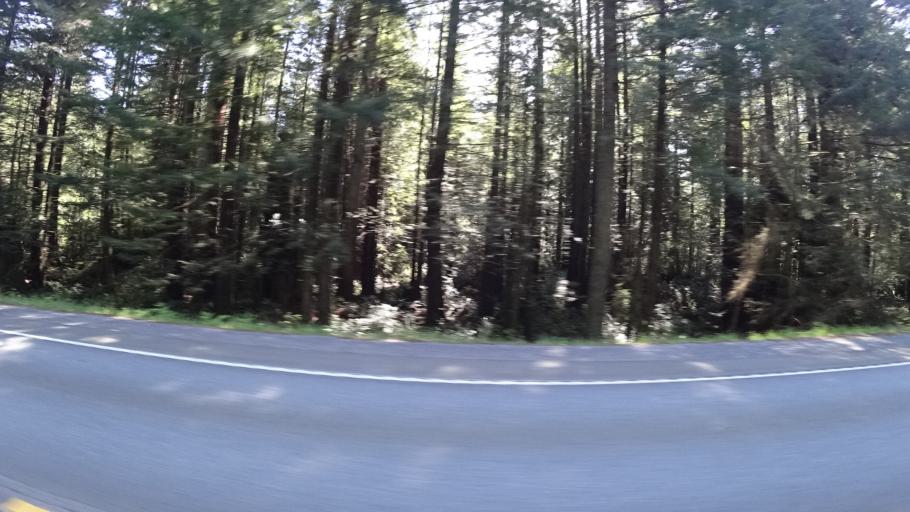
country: US
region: California
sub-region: Del Norte County
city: Bertsch-Oceanview
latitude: 41.8166
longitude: -124.1462
